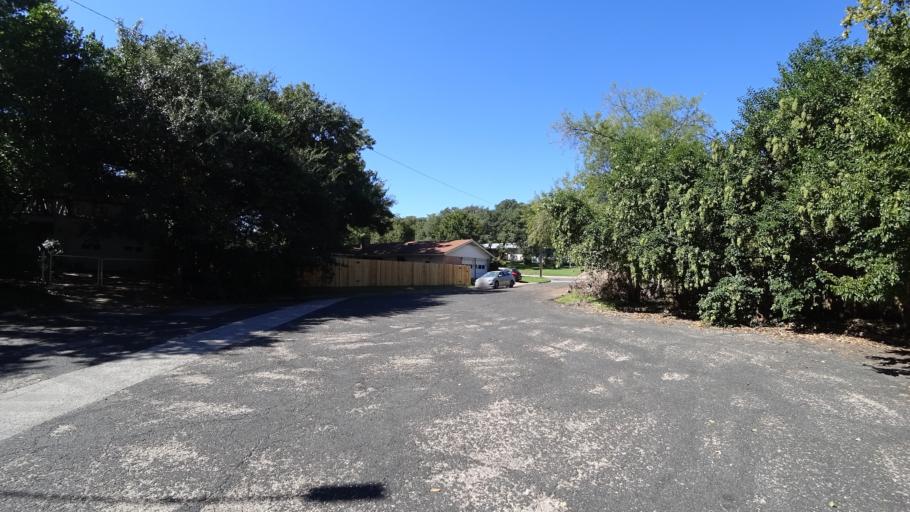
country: US
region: Texas
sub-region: Travis County
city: Austin
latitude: 30.2385
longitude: -97.7475
